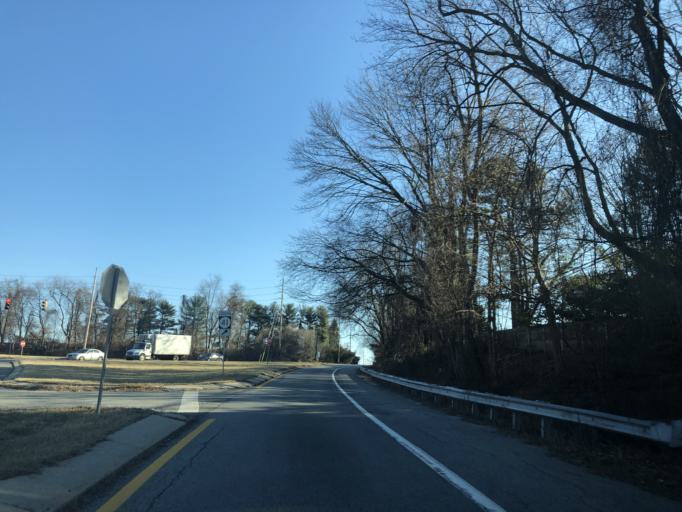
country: US
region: Delaware
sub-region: New Castle County
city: Hockessin
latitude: 39.7739
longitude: -75.6724
